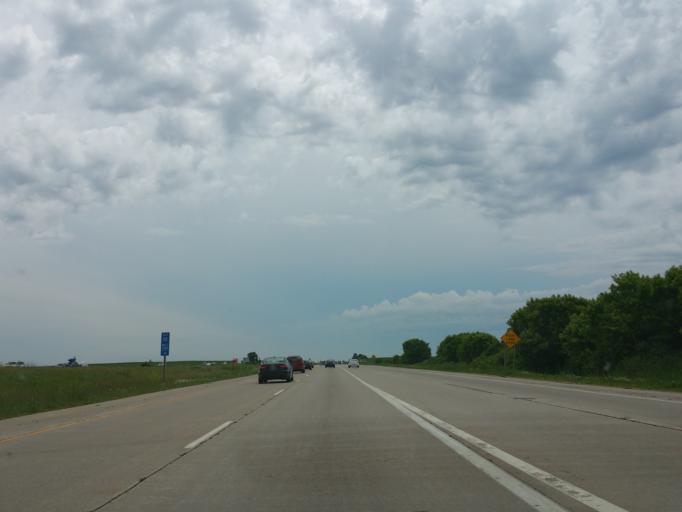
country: US
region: Wisconsin
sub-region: Columbia County
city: Portage
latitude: 43.4784
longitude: -89.4932
